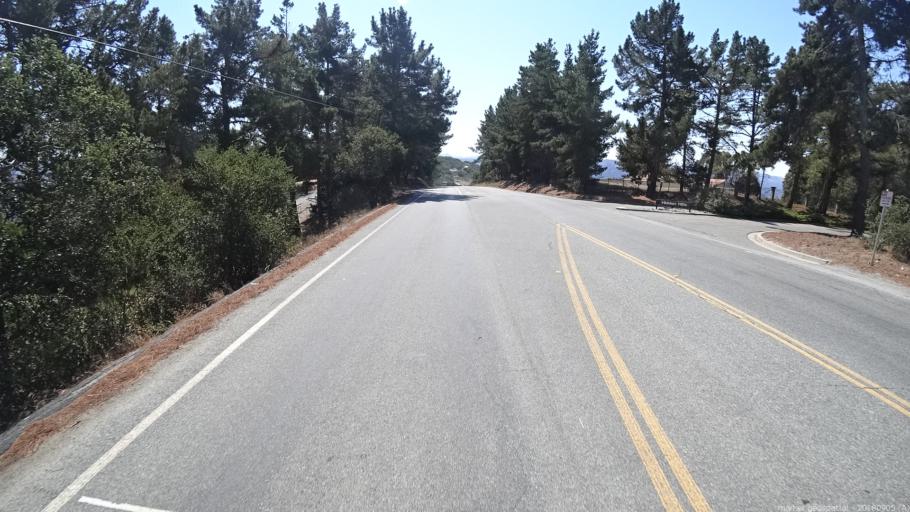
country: US
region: California
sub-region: Monterey County
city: Carmel Valley Village
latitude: 36.5419
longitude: -121.7536
